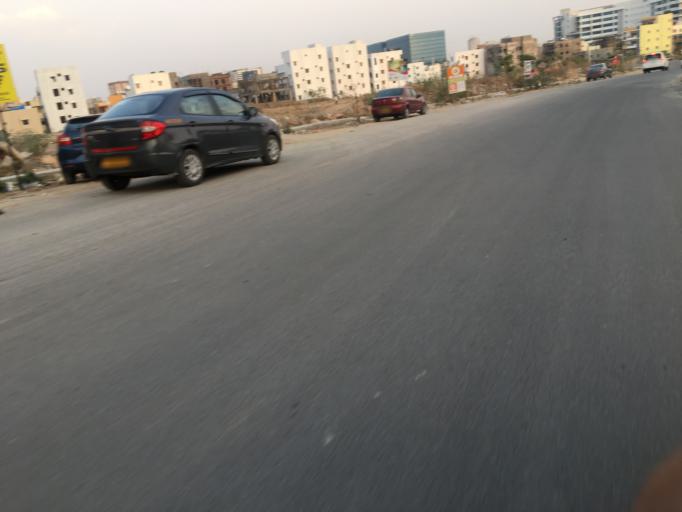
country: IN
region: Telangana
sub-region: Medak
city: Serilingampalle
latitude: 17.4319
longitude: 78.3311
